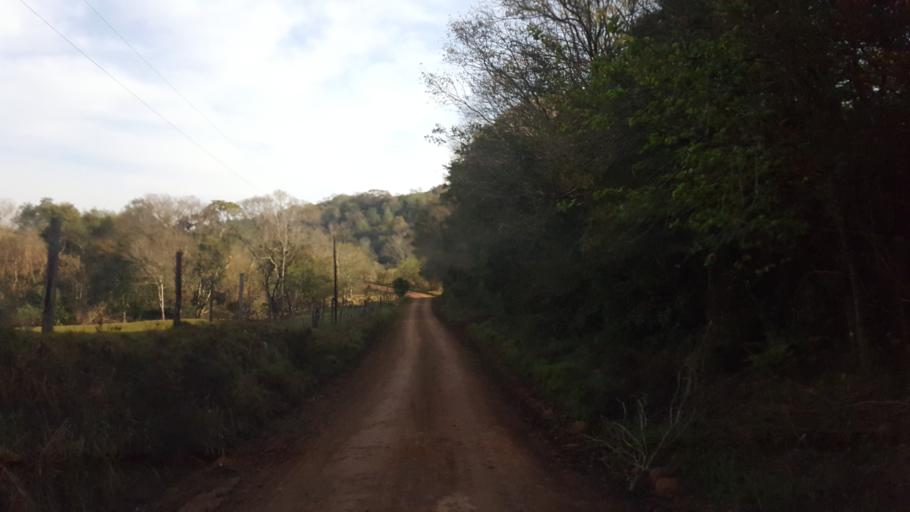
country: AR
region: Misiones
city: Capiovi
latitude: -26.9113
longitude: -55.0842
